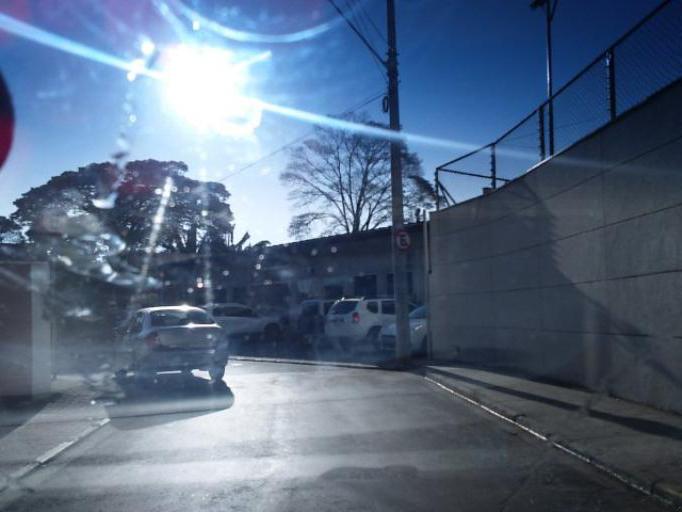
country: BR
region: Sao Paulo
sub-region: Sao Jose Dos Campos
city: Sao Jose dos Campos
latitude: -23.1962
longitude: -45.8986
